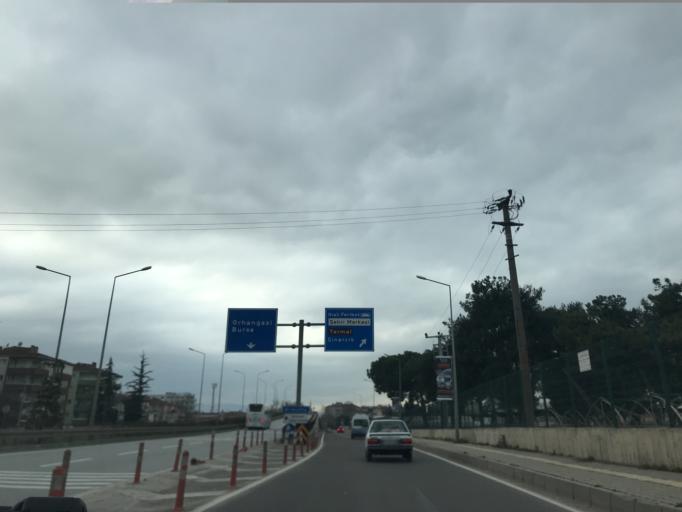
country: TR
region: Yalova
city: Yalova
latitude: 40.6579
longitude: 29.2877
